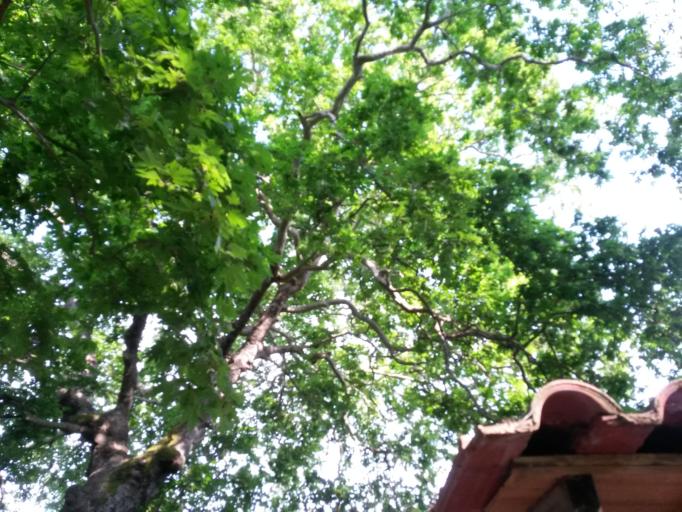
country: GR
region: North Aegean
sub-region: Nomos Lesvou
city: Agiasos
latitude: 39.1072
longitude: 26.3967
